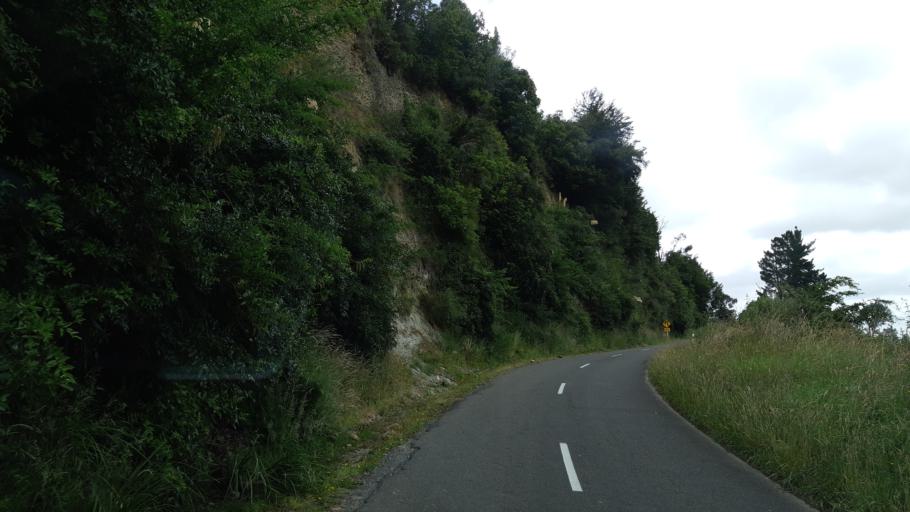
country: NZ
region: Manawatu-Wanganui
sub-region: Palmerston North City
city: Palmerston North
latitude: -39.9388
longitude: 175.9160
